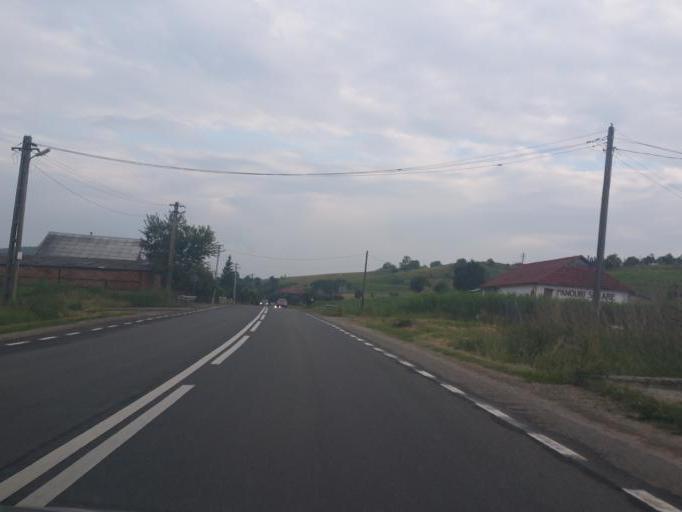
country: RO
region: Cluj
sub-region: Comuna Sanpaul
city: Sanpaul
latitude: 46.9124
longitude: 23.4176
